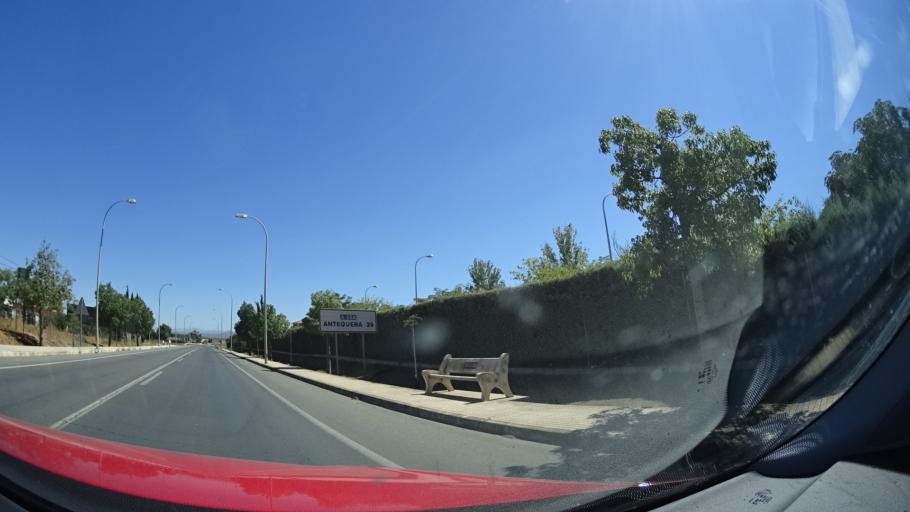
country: ES
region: Andalusia
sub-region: Provincia de Malaga
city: Campillos
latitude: 37.0512
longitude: -4.8580
